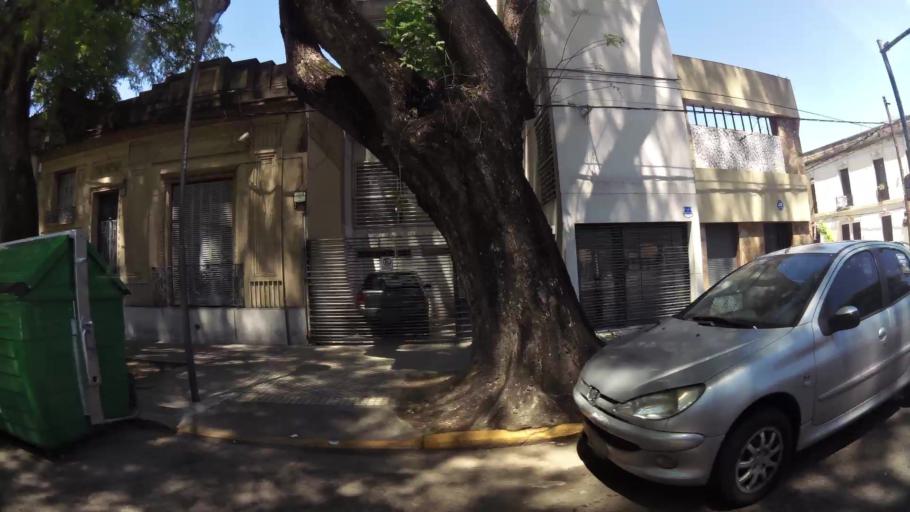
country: AR
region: Santa Fe
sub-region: Departamento de Rosario
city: Rosario
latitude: -32.9355
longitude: -60.6640
